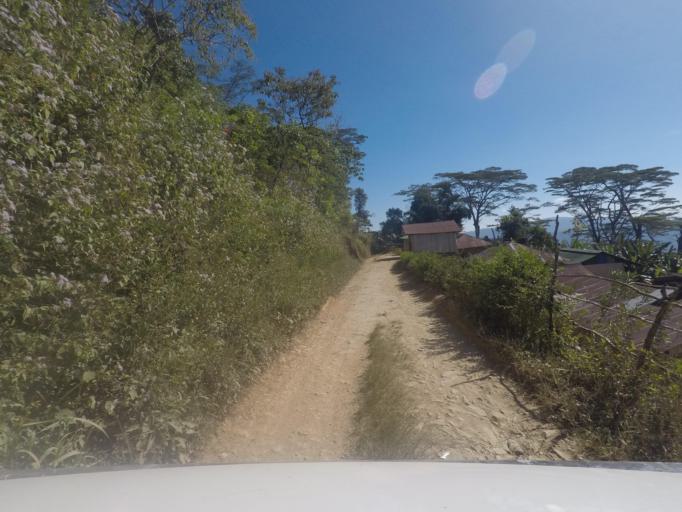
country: TL
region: Ermera
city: Gleno
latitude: -8.7350
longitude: 125.3436
